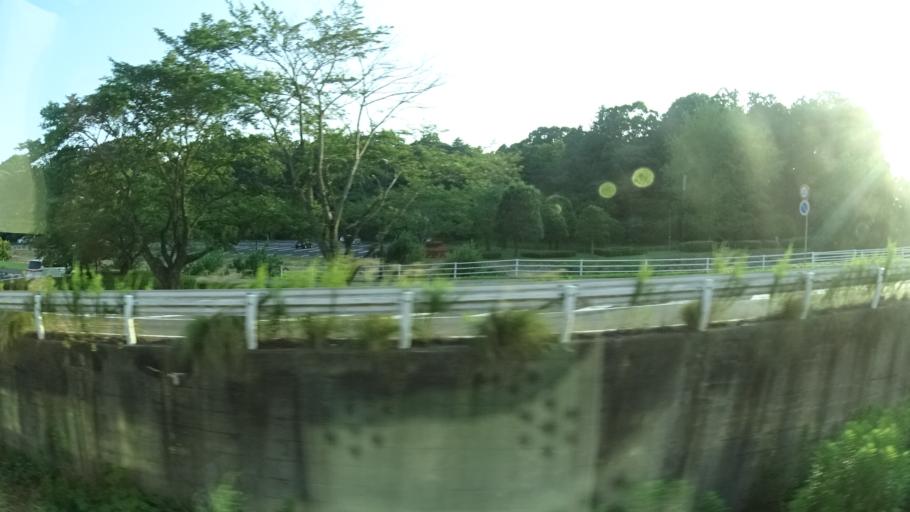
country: JP
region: Ibaraki
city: Mito-shi
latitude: 36.3761
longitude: 140.4491
